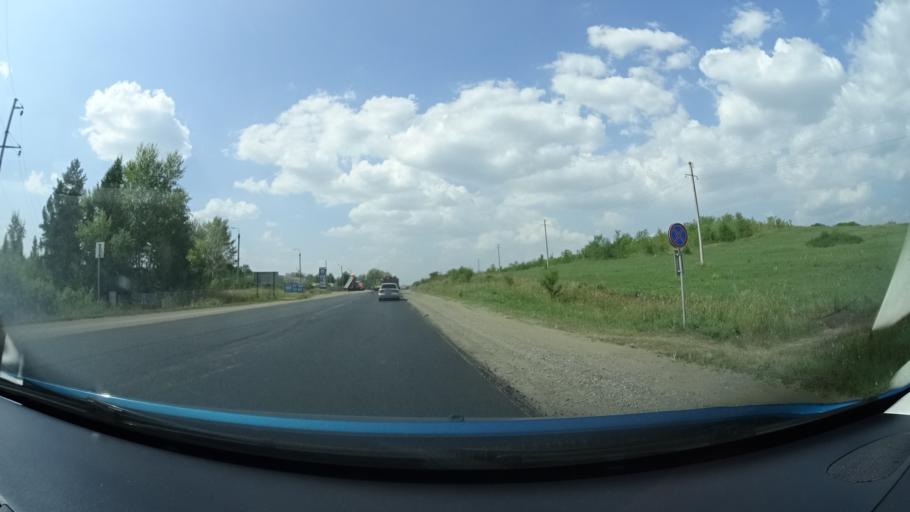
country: RU
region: Bashkortostan
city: Kandry
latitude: 54.5142
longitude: 54.0295
